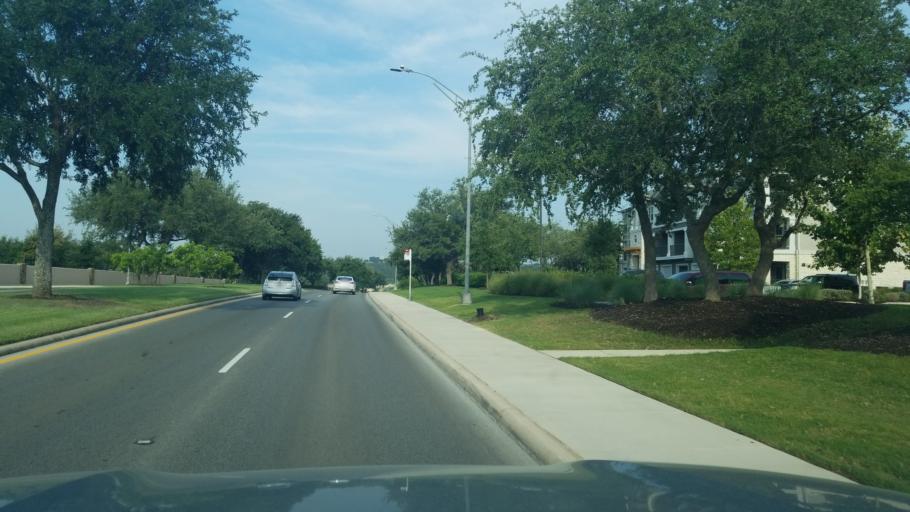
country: US
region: Texas
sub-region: Bexar County
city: Hollywood Park
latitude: 29.6447
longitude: -98.4719
